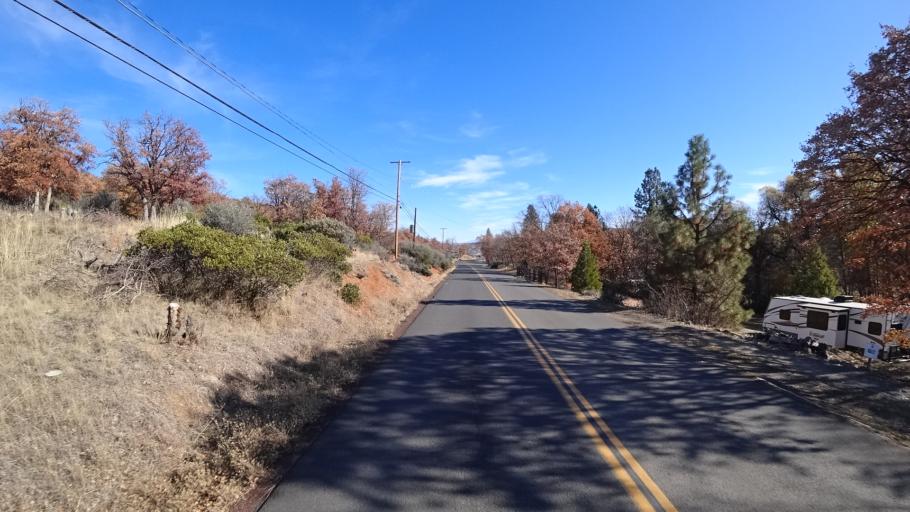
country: US
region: California
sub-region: Siskiyou County
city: Yreka
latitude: 41.7141
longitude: -122.6560
